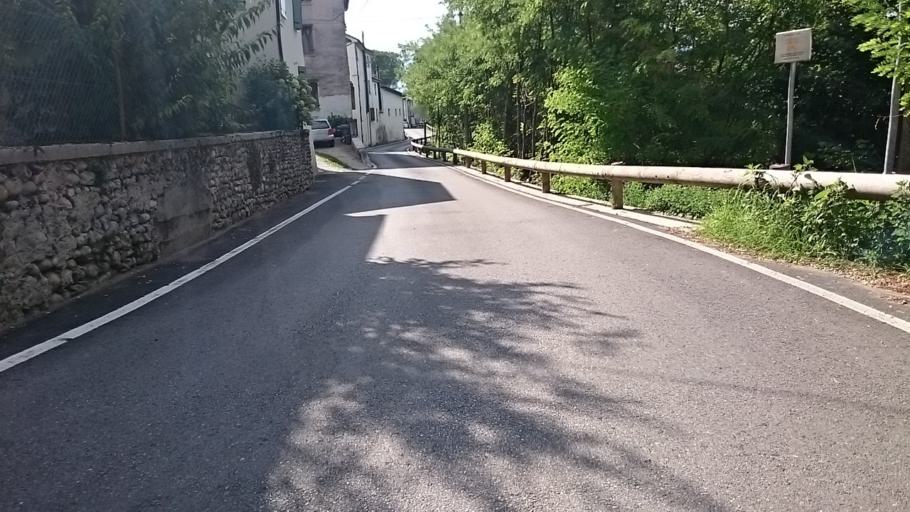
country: IT
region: Veneto
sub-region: Provincia di Treviso
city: Covolo-Levada
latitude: 45.8554
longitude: 12.0131
